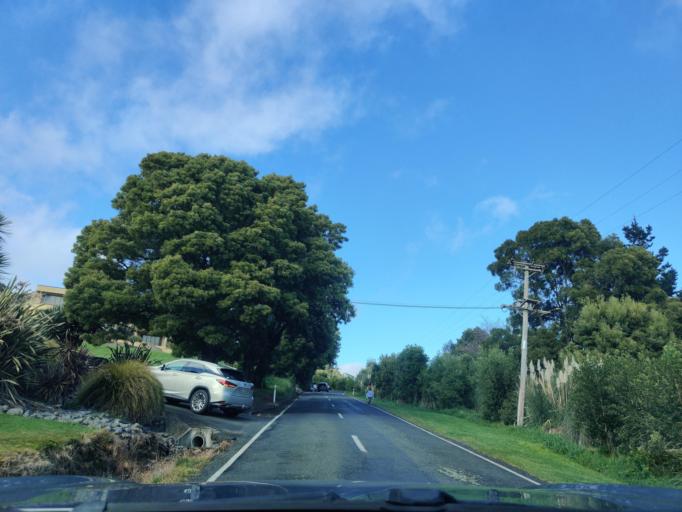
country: NZ
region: Hawke's Bay
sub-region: Hastings District
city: Hastings
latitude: -39.6913
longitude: 176.9004
